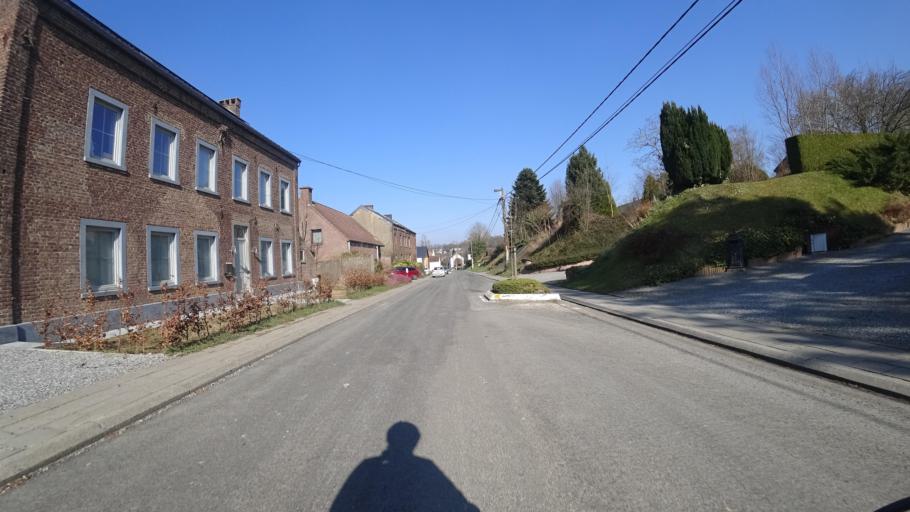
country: BE
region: Wallonia
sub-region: Province du Brabant Wallon
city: Mont-Saint-Guibert
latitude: 50.6377
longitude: 4.5948
